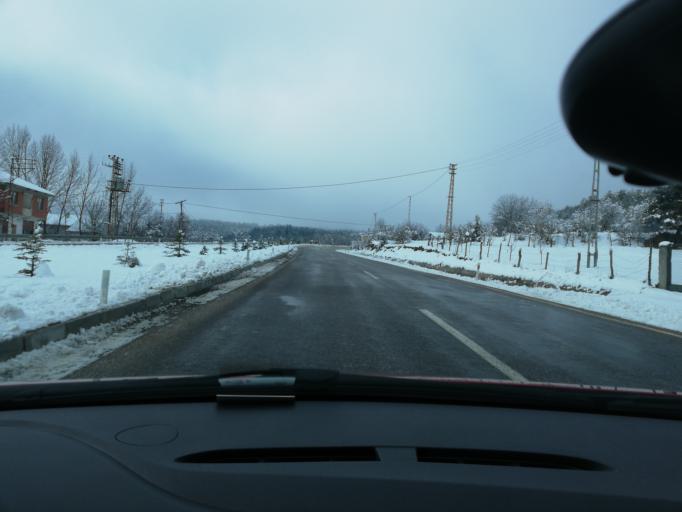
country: TR
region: Kastamonu
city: Ihsangazi
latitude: 41.3019
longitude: 33.5414
